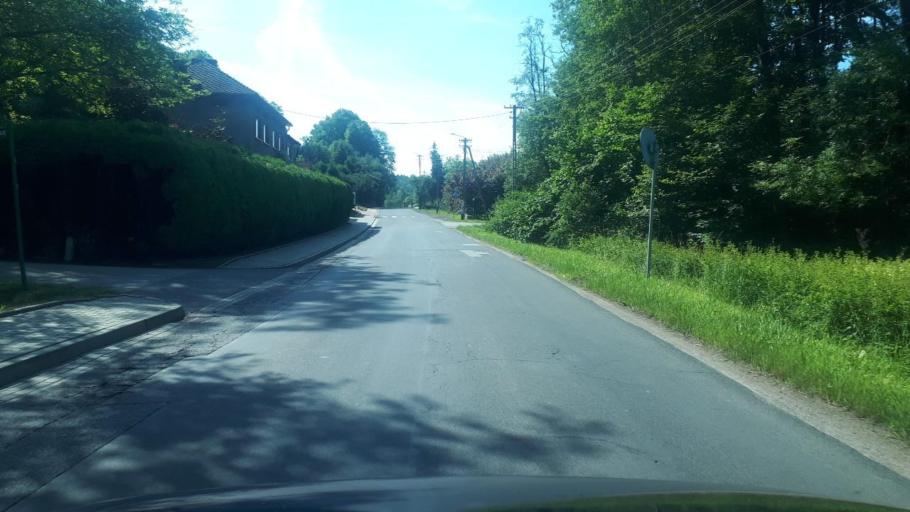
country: PL
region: Silesian Voivodeship
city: Janowice
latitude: 49.9062
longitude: 19.1156
